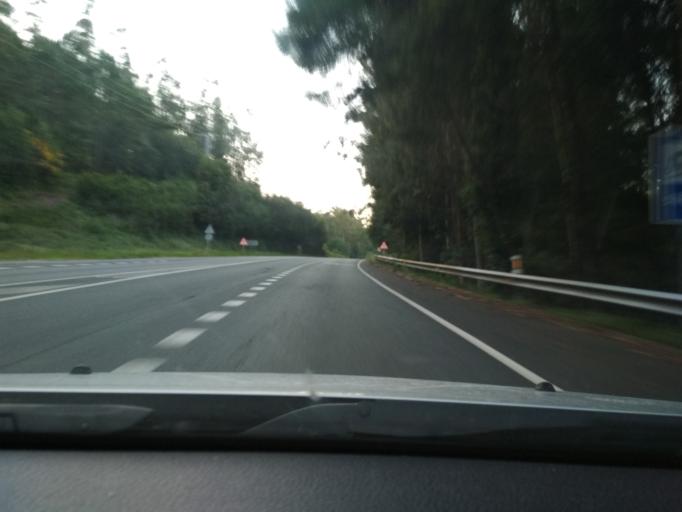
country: ES
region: Galicia
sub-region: Provincia de Pontevedra
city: Caldas de Reis
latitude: 42.6293
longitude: -8.6489
